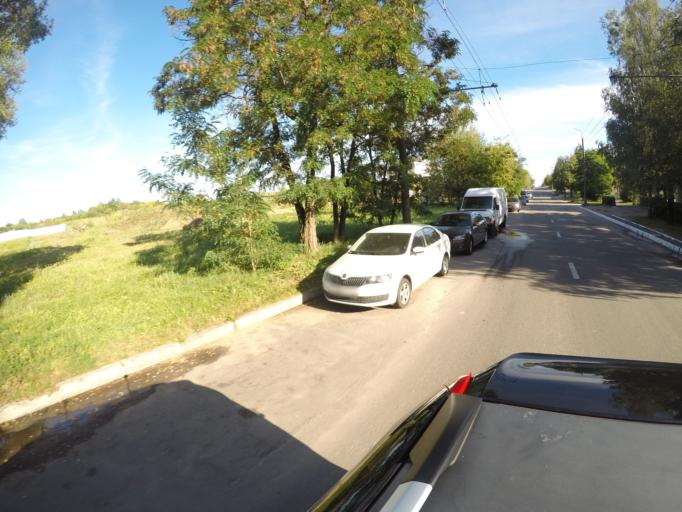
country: BY
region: Grodnenskaya
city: Hrodna
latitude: 53.7130
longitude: 23.8259
